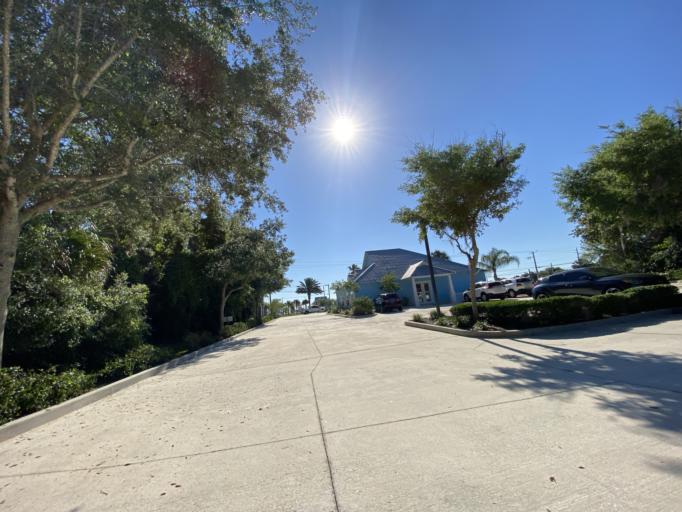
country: US
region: Florida
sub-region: Volusia County
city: Port Orange
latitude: 29.1483
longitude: -80.9908
